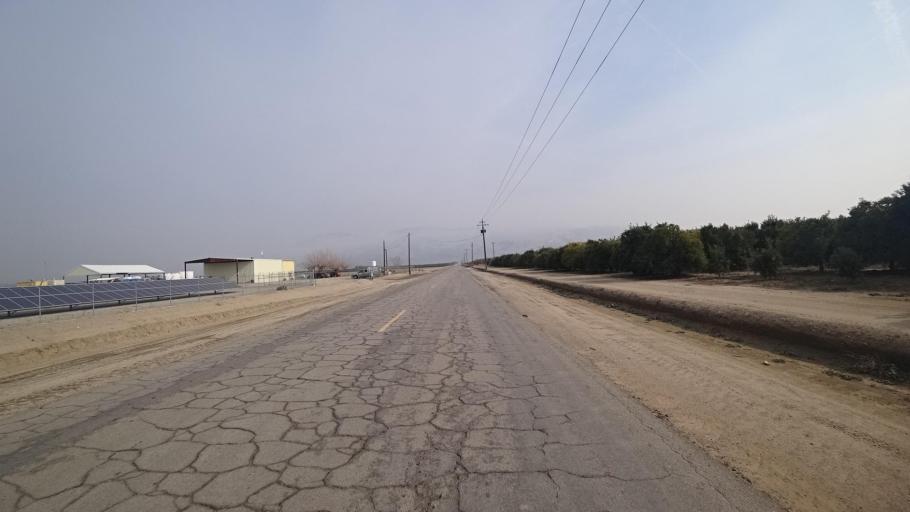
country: US
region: California
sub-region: Kern County
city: Arvin
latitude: 35.1510
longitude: -118.8431
